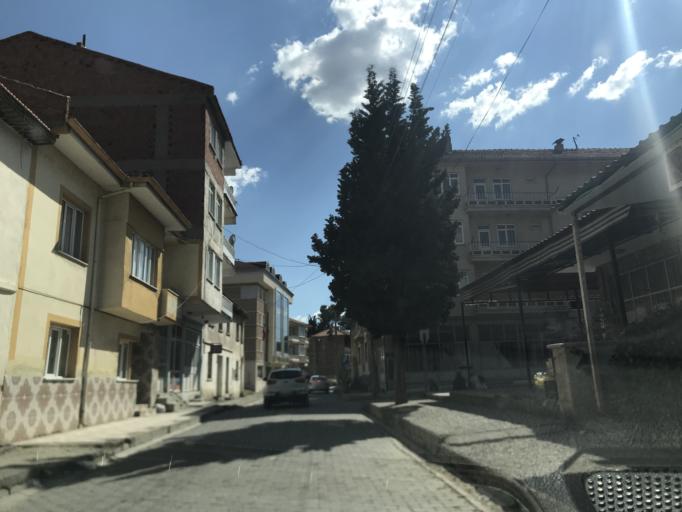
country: TR
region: Denizli
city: Civril
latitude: 38.3005
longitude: 29.7421
